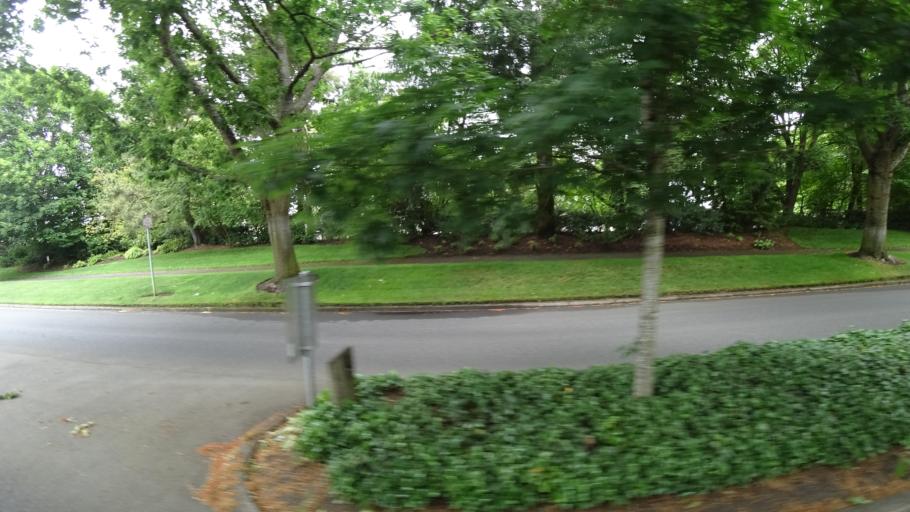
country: US
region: Washington
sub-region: Clark County
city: Vancouver
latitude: 45.6065
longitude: -122.6707
